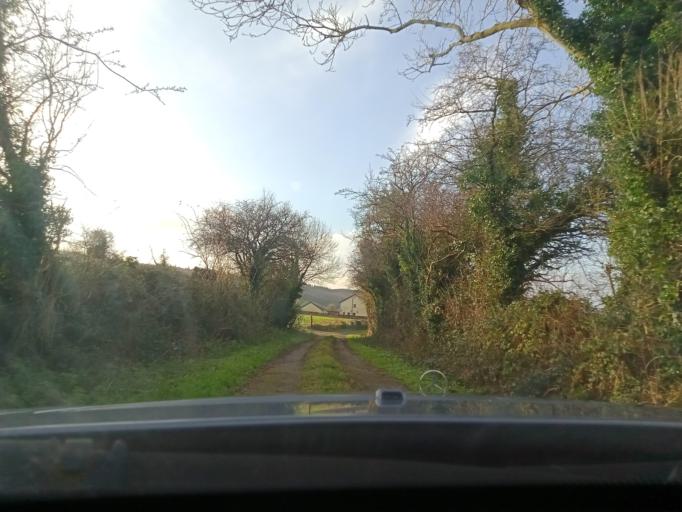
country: IE
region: Leinster
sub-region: Kilkenny
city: Callan
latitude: 52.4815
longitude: -7.4356
